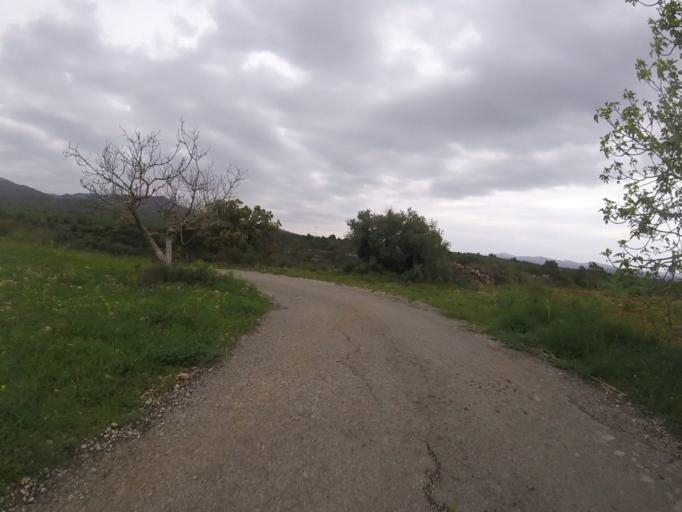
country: ES
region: Valencia
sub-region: Provincia de Castello
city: Cuevas de Vinroma
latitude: 40.2914
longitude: 0.0863
